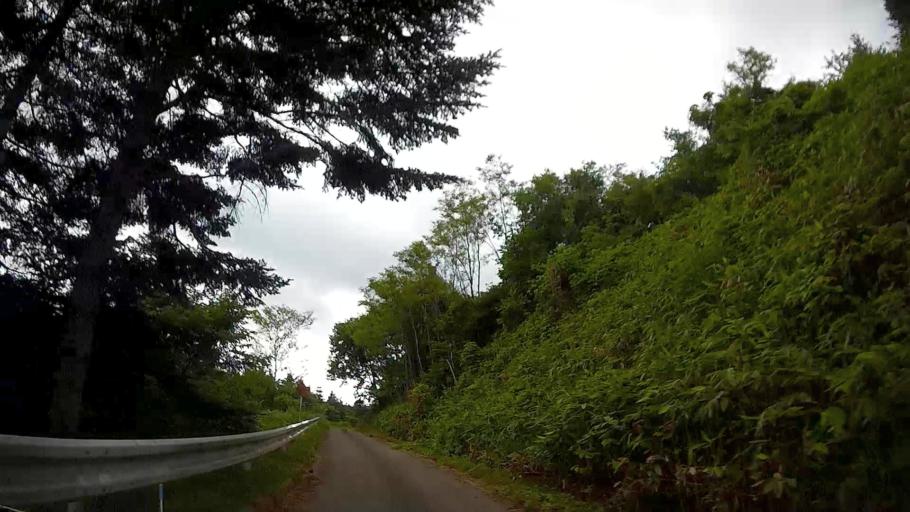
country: JP
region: Hokkaido
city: Nanae
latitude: 42.1265
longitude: 140.4260
